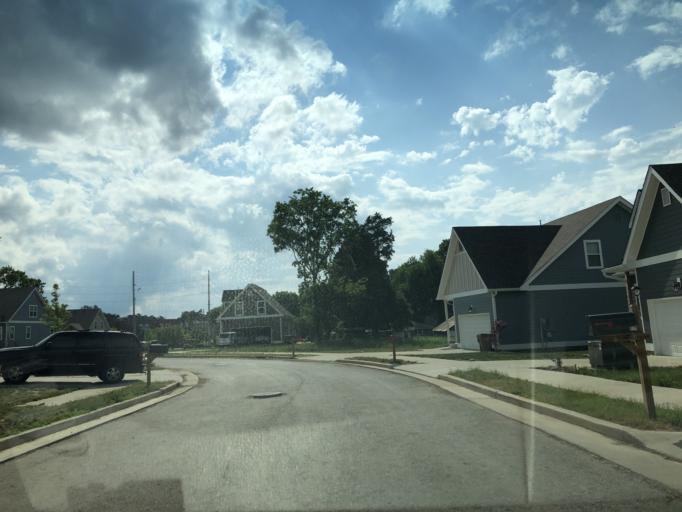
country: US
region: Tennessee
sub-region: Davidson County
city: Goodlettsville
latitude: 36.2747
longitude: -86.7009
